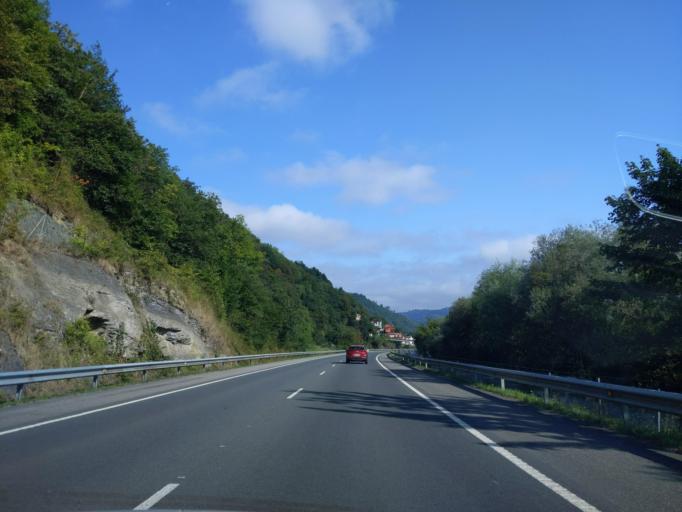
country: ES
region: Asturias
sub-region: Province of Asturias
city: Pola de Laviana
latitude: 43.2402
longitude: -5.5655
